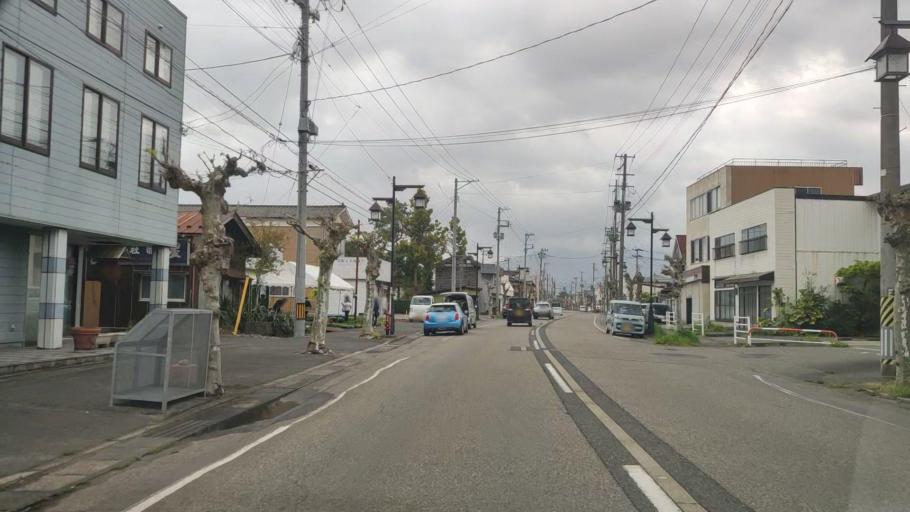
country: JP
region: Niigata
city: Gosen
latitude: 37.7379
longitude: 139.1811
